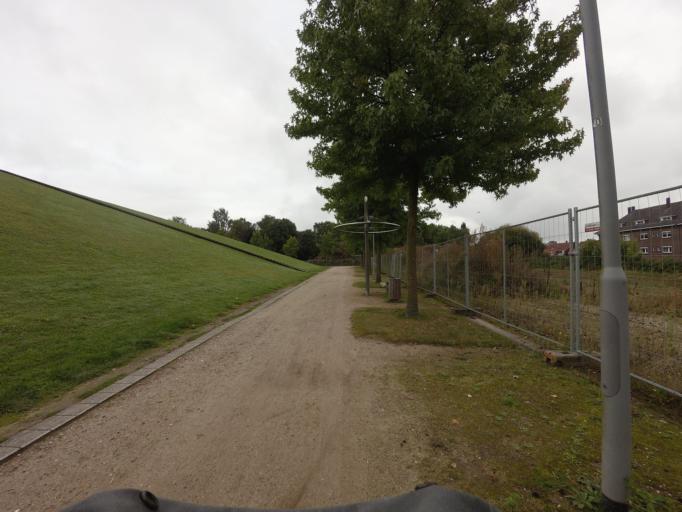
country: DE
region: North Rhine-Westphalia
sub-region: Regierungsbezirk Munster
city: Gronau
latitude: 52.2128
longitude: 7.0289
